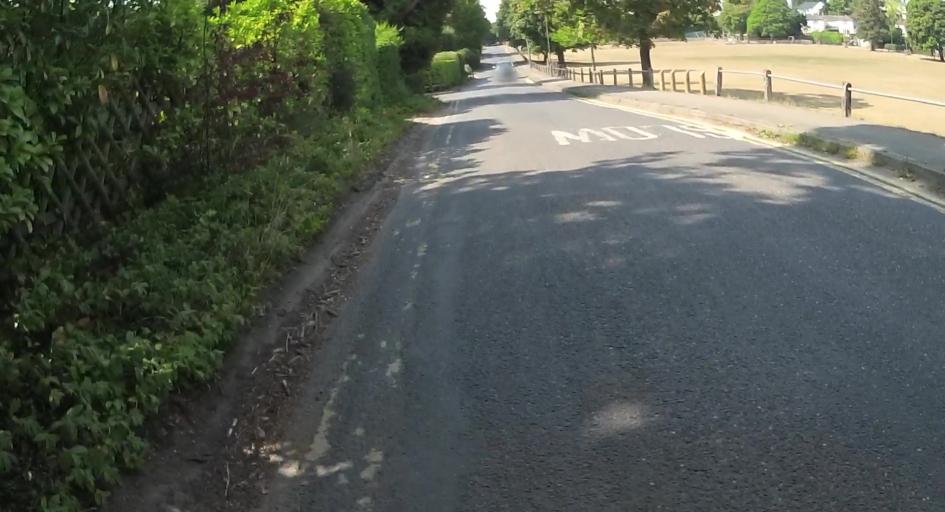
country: GB
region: England
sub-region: Surrey
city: Farnham
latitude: 51.1947
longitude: -0.7872
